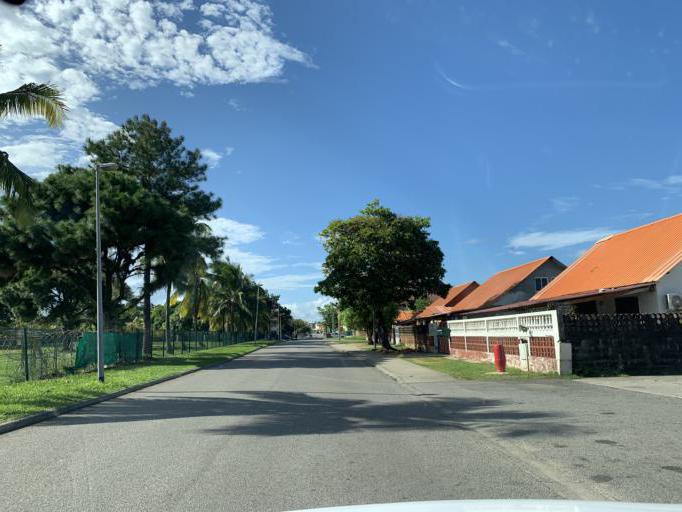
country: GF
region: Guyane
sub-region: Guyane
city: Kourou
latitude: 5.1731
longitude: -52.6472
